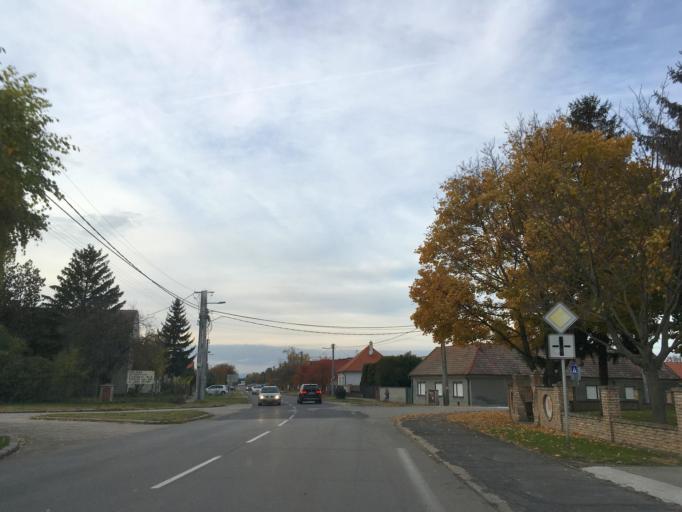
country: SK
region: Trnavsky
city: Samorin
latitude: 48.0997
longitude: 17.3529
